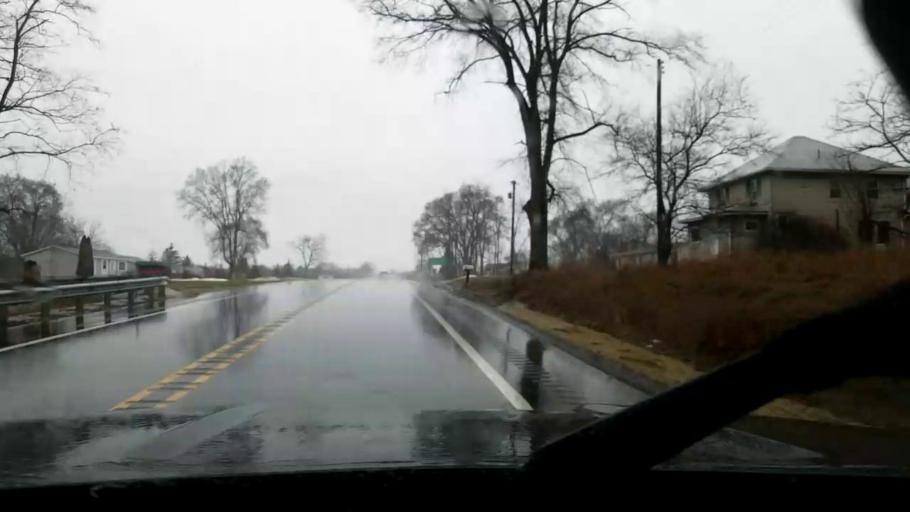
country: US
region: Michigan
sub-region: Jackson County
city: Michigan Center
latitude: 42.1867
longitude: -84.3028
